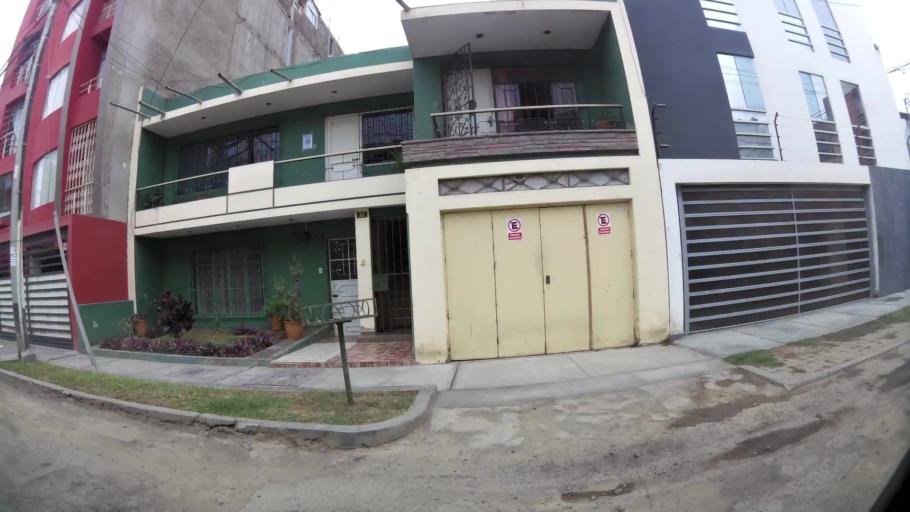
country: PE
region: La Libertad
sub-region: Provincia de Trujillo
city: Buenos Aires
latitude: -8.1321
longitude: -79.0435
